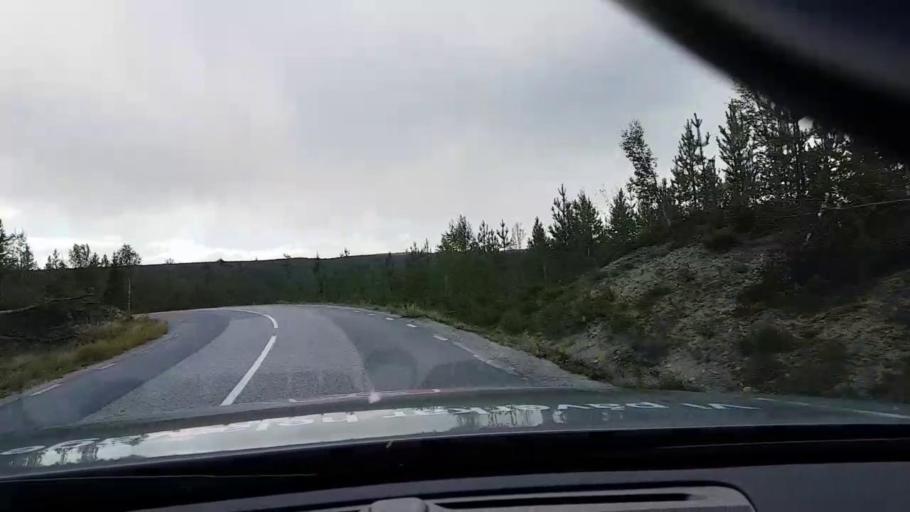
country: SE
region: Vaesterbotten
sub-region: Asele Kommun
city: Asele
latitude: 63.8045
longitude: 17.5469
